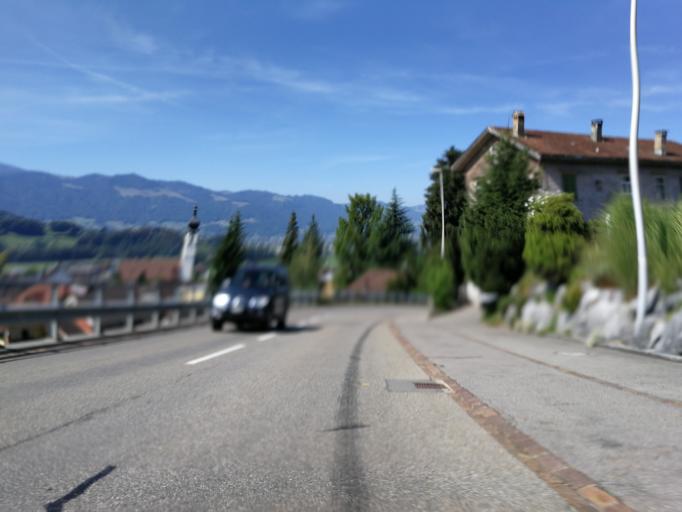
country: CH
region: Saint Gallen
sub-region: Wahlkreis See-Gaster
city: Kaltbrunn
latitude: 47.2169
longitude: 9.0279
